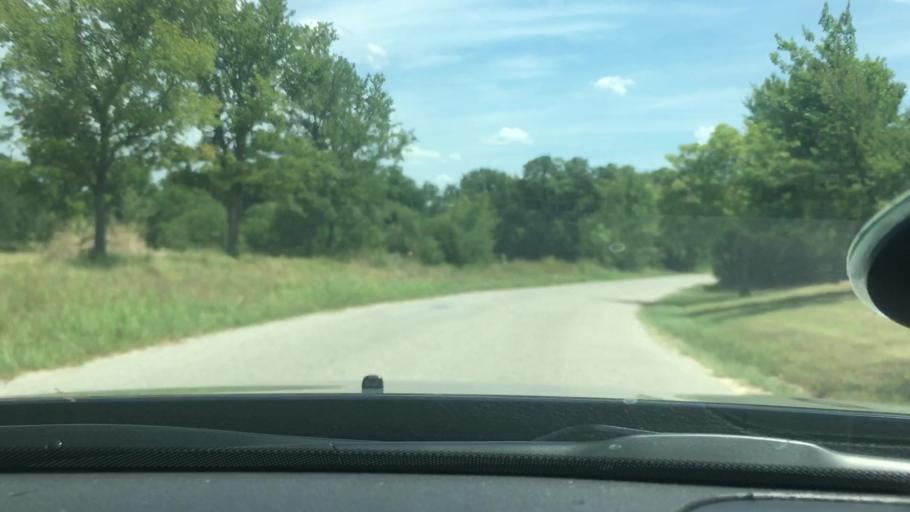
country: US
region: Oklahoma
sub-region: Carter County
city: Ardmore
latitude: 34.0725
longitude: -97.1849
